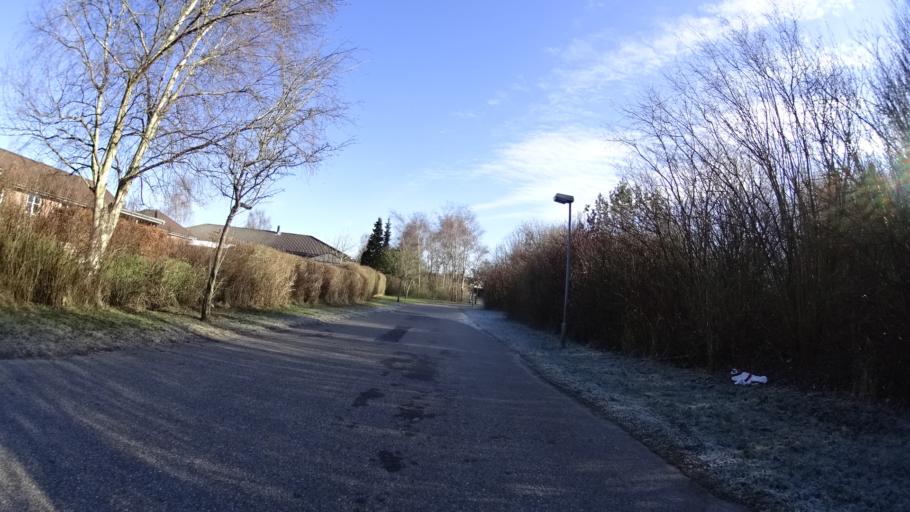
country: DK
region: Central Jutland
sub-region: Arhus Kommune
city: Kolt
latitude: 56.1077
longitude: 10.0833
